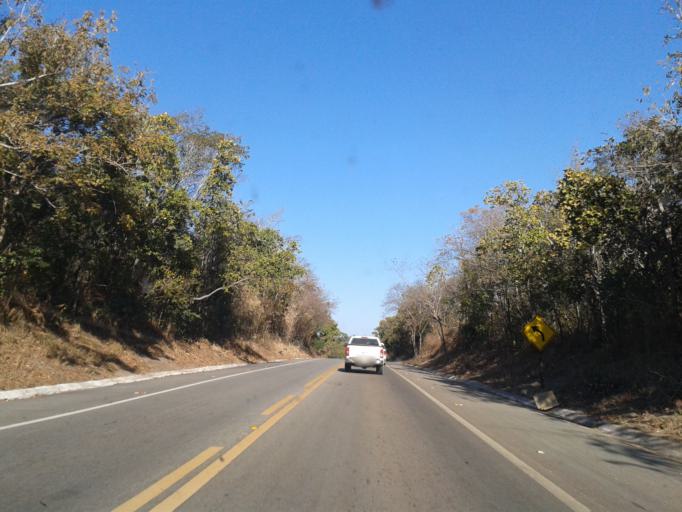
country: BR
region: Goias
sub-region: Itapirapua
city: Itapirapua
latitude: -15.3251
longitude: -50.4314
